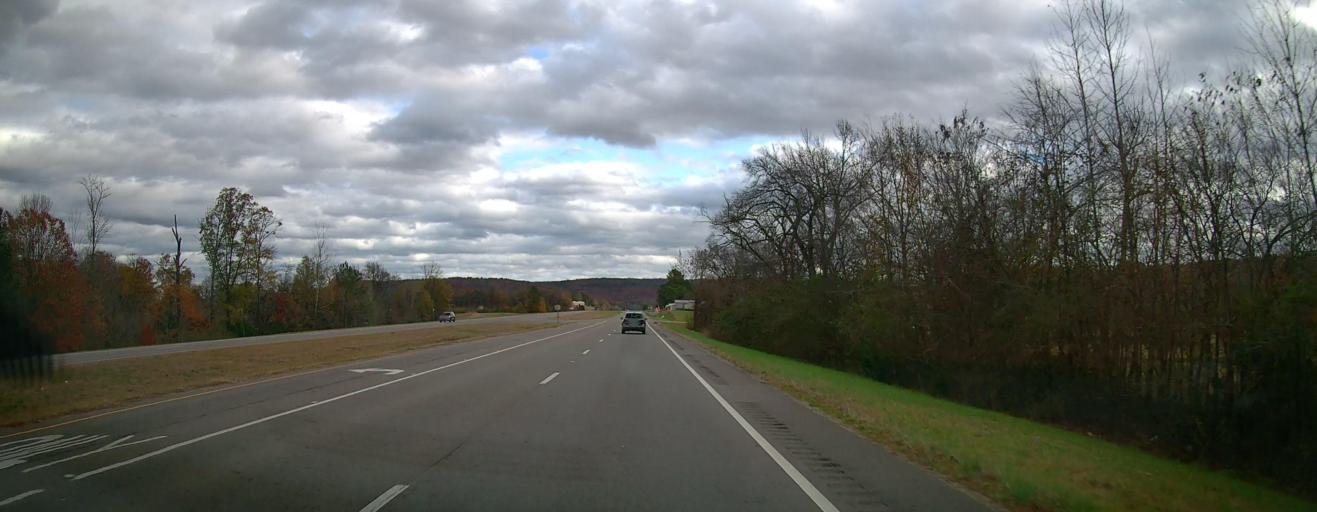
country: US
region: Alabama
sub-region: Morgan County
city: Danville
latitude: 34.3392
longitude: -87.0236
